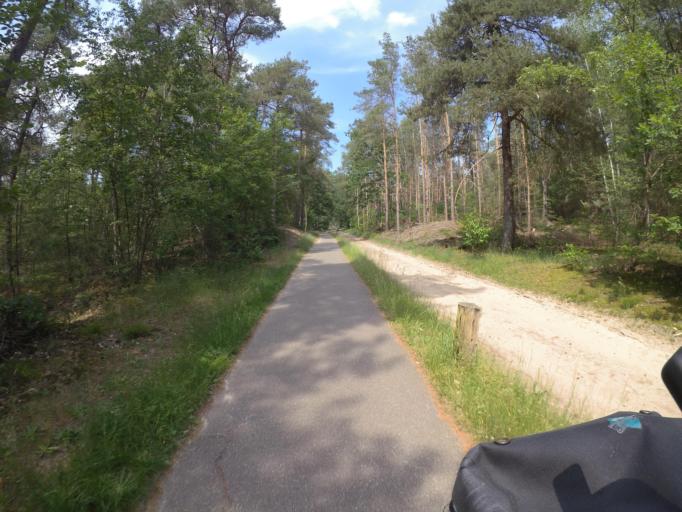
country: NL
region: Overijssel
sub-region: Gemeente Twenterand
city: Den Ham
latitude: 52.3764
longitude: 6.4325
